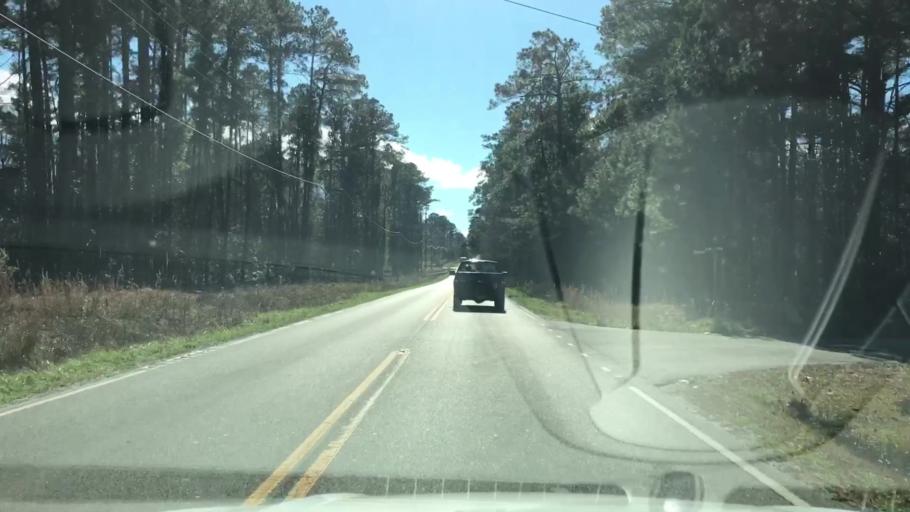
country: US
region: South Carolina
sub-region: Dorchester County
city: Summerville
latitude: 33.0536
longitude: -80.2402
